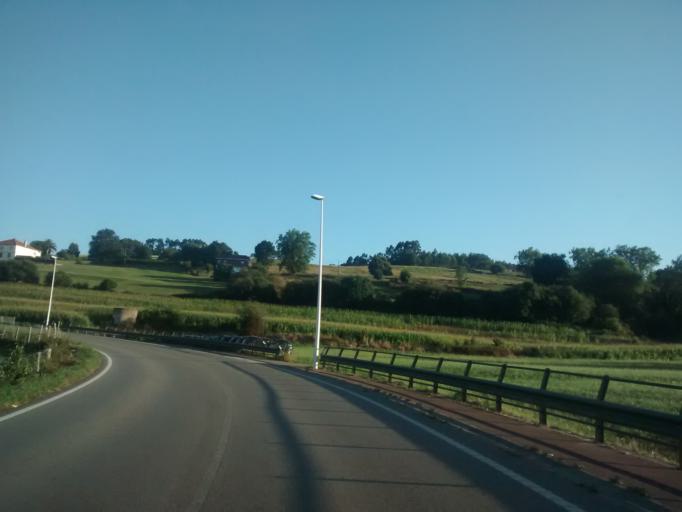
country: ES
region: Cantabria
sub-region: Provincia de Cantabria
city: San Miguel de Meruelo
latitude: 43.4480
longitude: -3.5752
